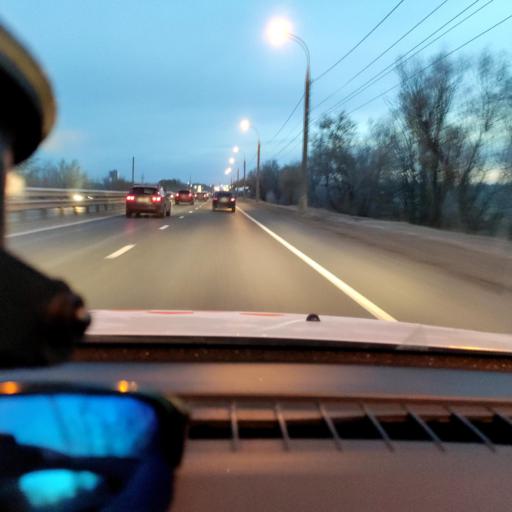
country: RU
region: Samara
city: Samara
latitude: 53.1205
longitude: 50.1683
